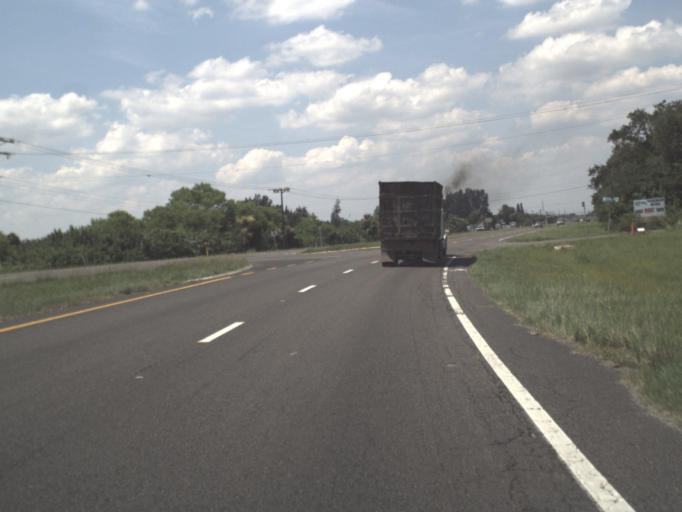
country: US
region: Florida
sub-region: Hillsborough County
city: Progress Village
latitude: 27.8931
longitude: -82.4016
